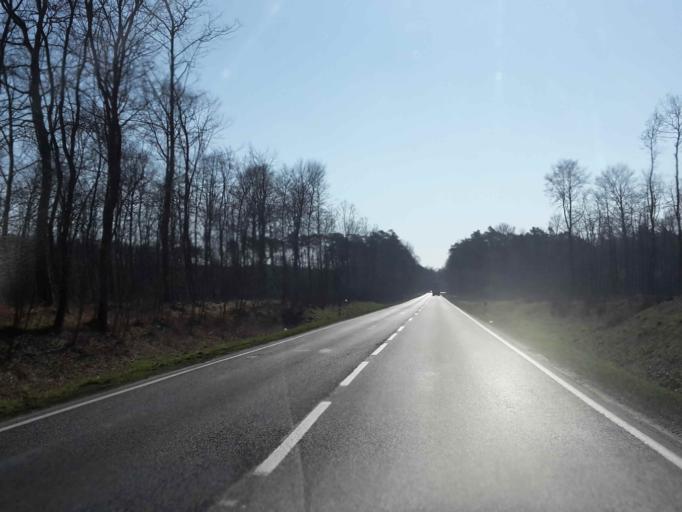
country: PL
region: Greater Poland Voivodeship
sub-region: Powiat nowotomyski
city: Nowy Tomysl
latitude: 52.3536
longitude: 16.1000
